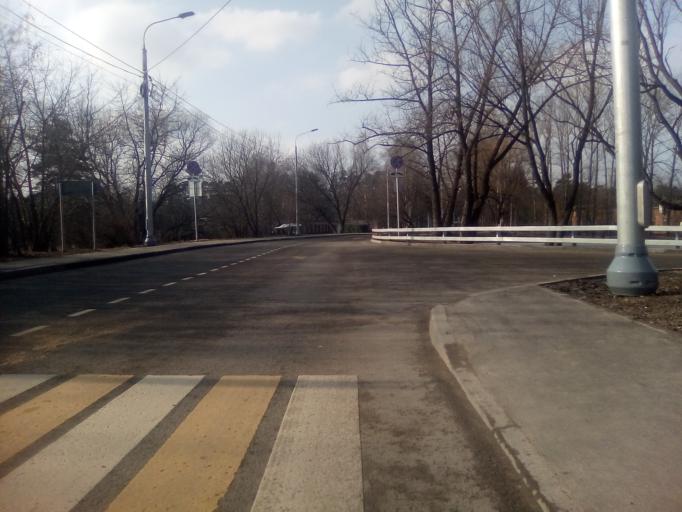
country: RU
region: Moscow
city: Novo-Peredelkino
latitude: 55.6580
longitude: 37.3560
